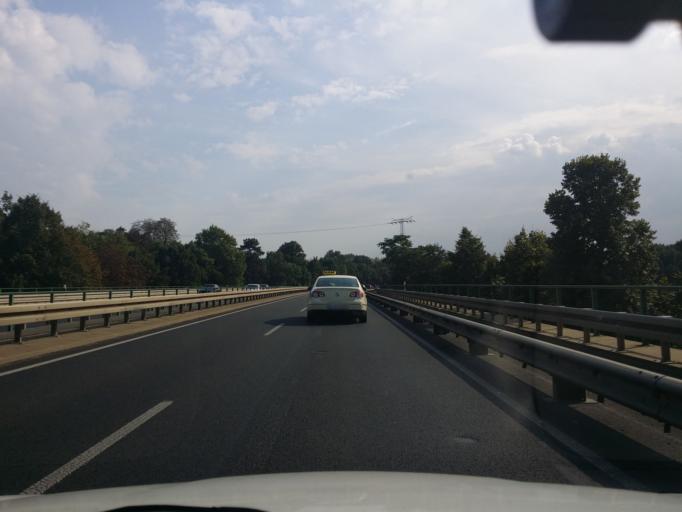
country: DE
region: Saxony
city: Markkleeberg
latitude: 51.2837
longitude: 12.3815
